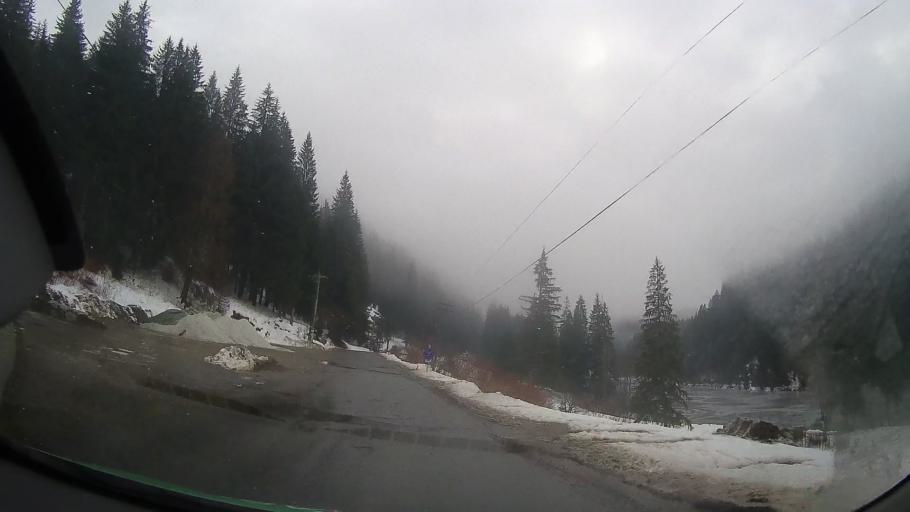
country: RO
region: Neamt
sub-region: Comuna Bicaz Chei
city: Bicaz Chei
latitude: 46.7896
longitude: 25.7885
